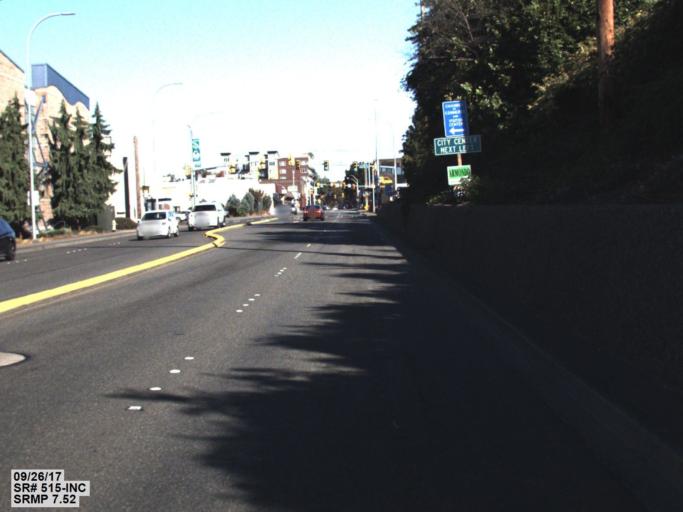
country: US
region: Washington
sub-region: King County
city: Renton
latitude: 47.4771
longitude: -122.2043
